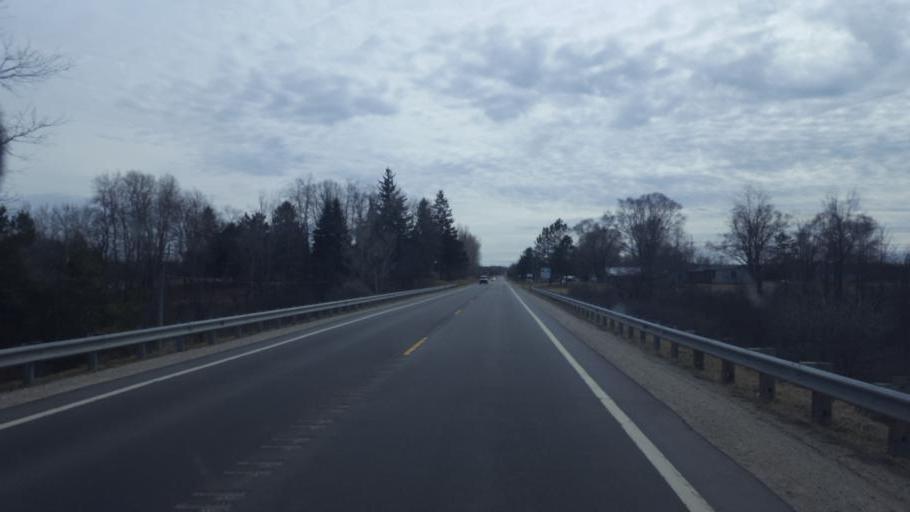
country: US
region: Michigan
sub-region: Isabella County
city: Lake Isabella
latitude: 43.7267
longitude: -85.1469
